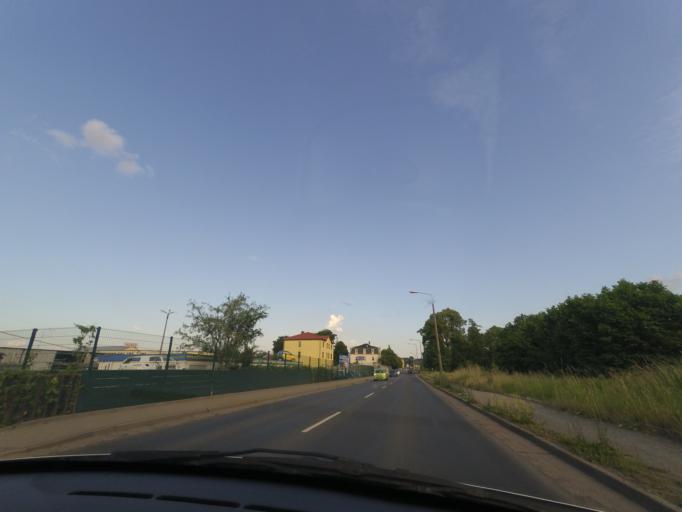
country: DE
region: Saxony
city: Dohna
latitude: 50.9917
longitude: 13.8078
